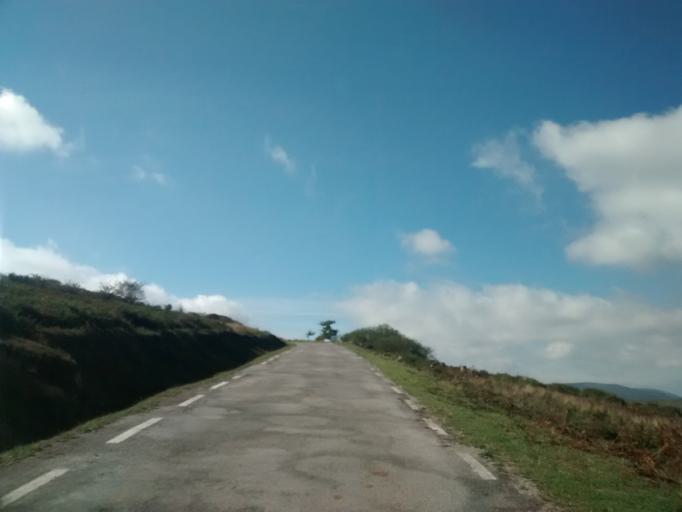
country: ES
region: Castille and Leon
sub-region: Provincia de Burgos
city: Arija
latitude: 42.9263
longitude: -3.9914
